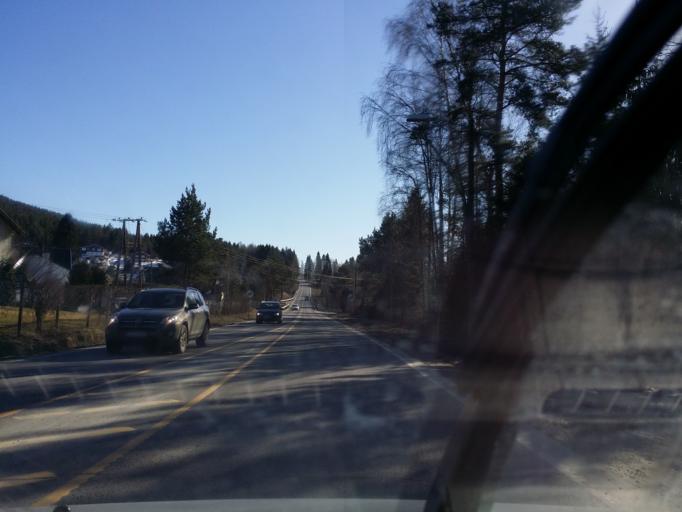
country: NO
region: Buskerud
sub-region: Ringerike
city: Honefoss
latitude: 60.2703
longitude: 10.1842
